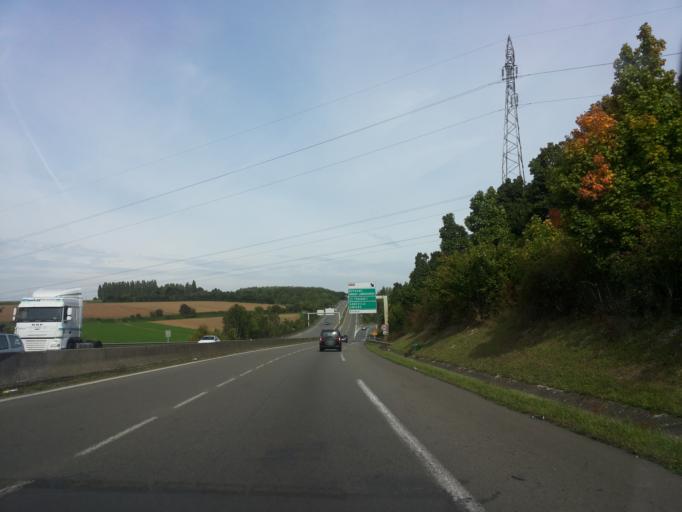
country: FR
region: Nord-Pas-de-Calais
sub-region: Departement du Pas-de-Calais
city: Saint-Nicolas
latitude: 50.3126
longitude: 2.7762
